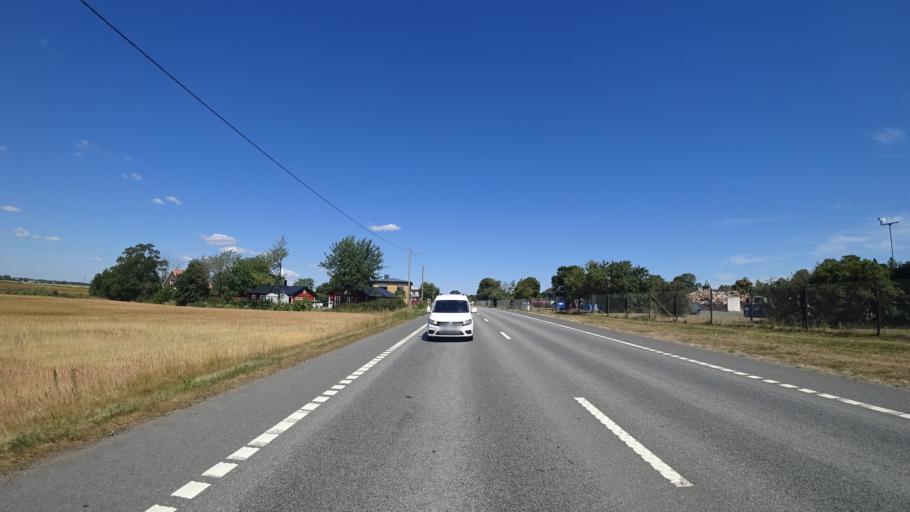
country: SE
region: Skane
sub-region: Kristianstads Kommun
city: Kristianstad
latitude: 56.0476
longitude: 14.0884
